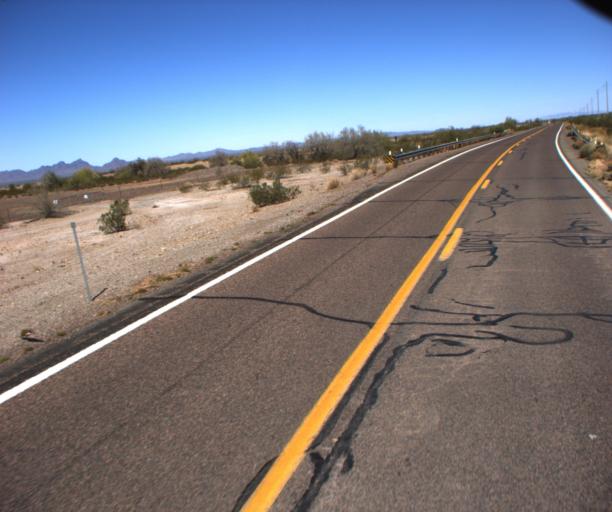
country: US
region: Arizona
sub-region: La Paz County
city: Salome
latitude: 33.7637
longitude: -113.7854
